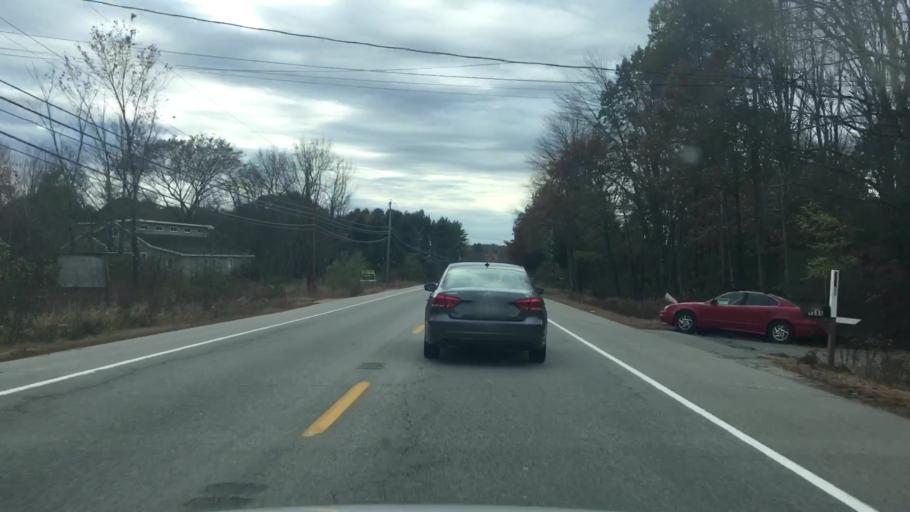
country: US
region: Maine
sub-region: York County
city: West Kennebunk
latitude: 43.4792
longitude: -70.6134
